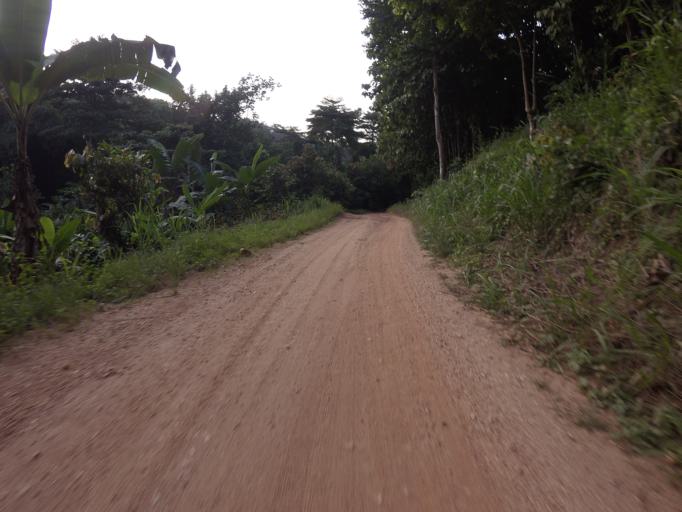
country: GH
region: Volta
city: Kpandu
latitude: 6.8806
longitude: 0.4381
